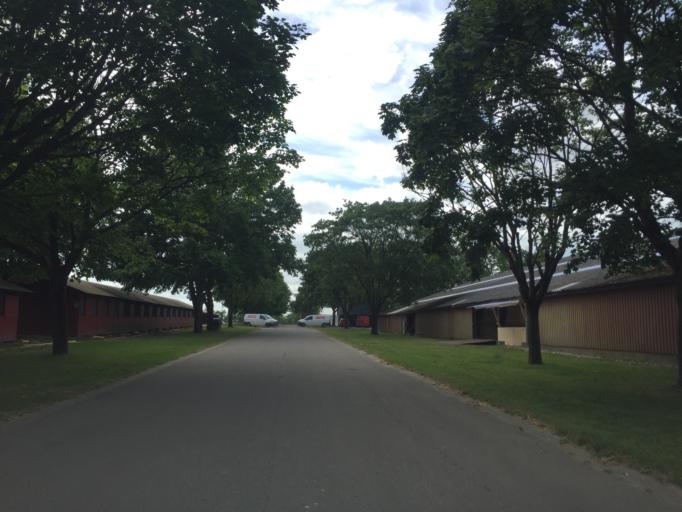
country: DK
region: Zealand
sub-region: Roskilde Kommune
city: Roskilde
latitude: 55.6202
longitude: 12.0829
